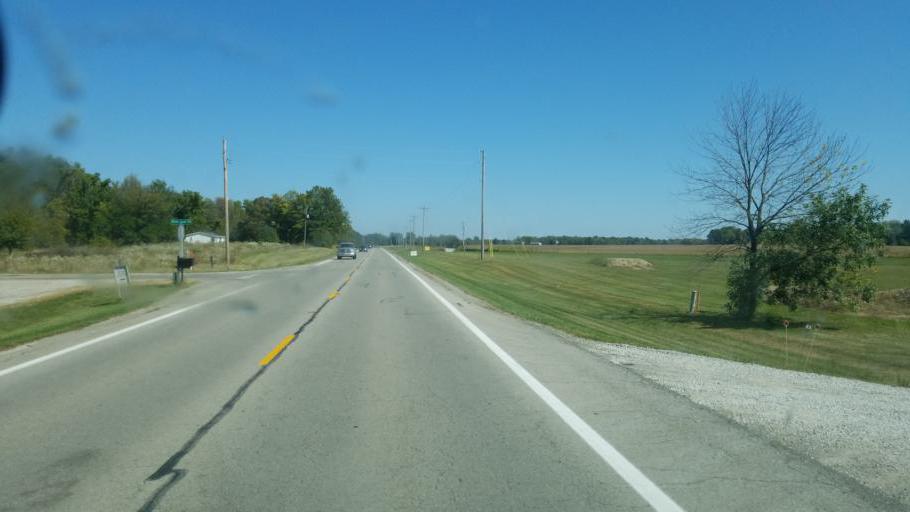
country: US
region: Ohio
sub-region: Morrow County
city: Mount Gilead
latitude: 40.6524
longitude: -82.8908
